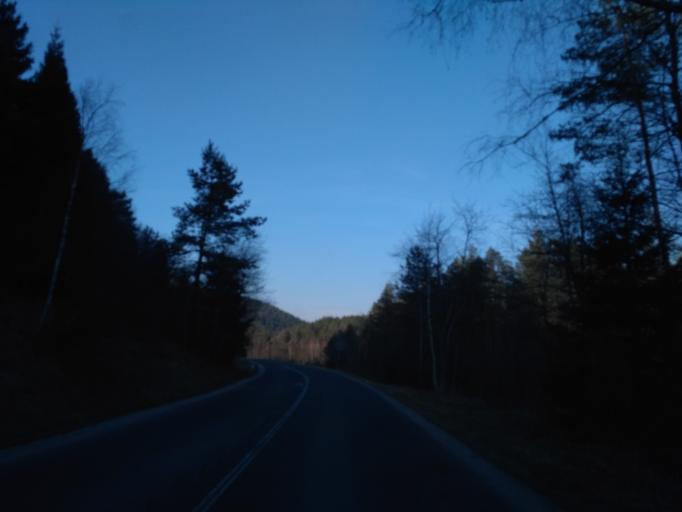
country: SK
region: Kosicky
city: Medzev
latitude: 48.7755
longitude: 20.7871
